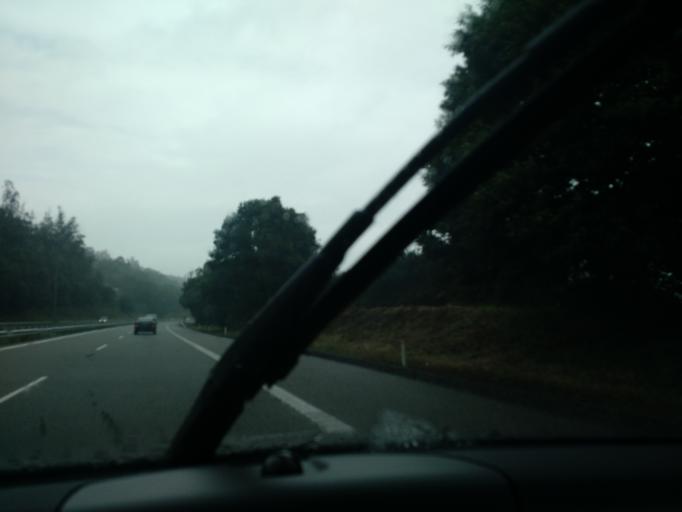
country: ES
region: Galicia
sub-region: Provincia da Coruna
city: Abegondo
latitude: 43.1826
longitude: -8.3108
